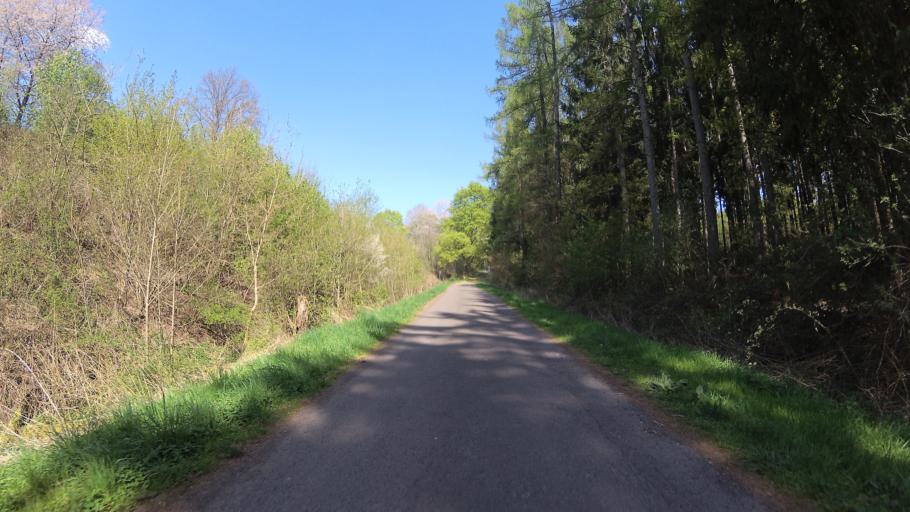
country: DE
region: Saarland
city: Ottweiler
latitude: 49.4156
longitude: 7.1916
